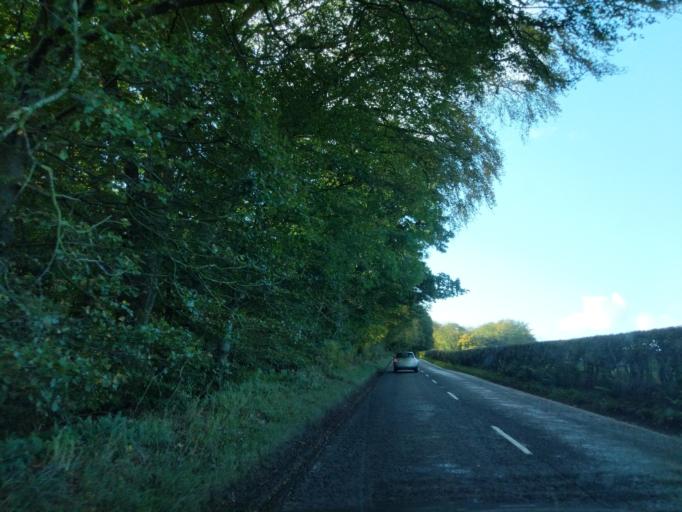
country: GB
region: Scotland
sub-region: Dumfries and Galloway
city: Castle Douglas
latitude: 54.9797
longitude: -3.8741
